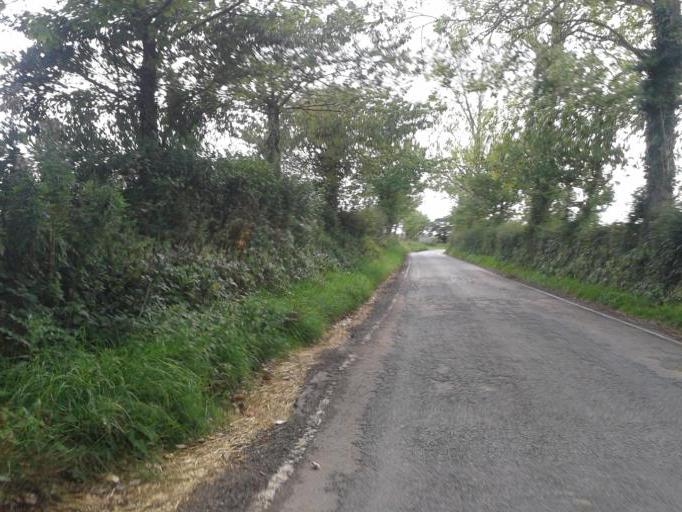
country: GB
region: England
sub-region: Cambridgeshire
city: Duxford
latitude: 52.0031
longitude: 0.1162
